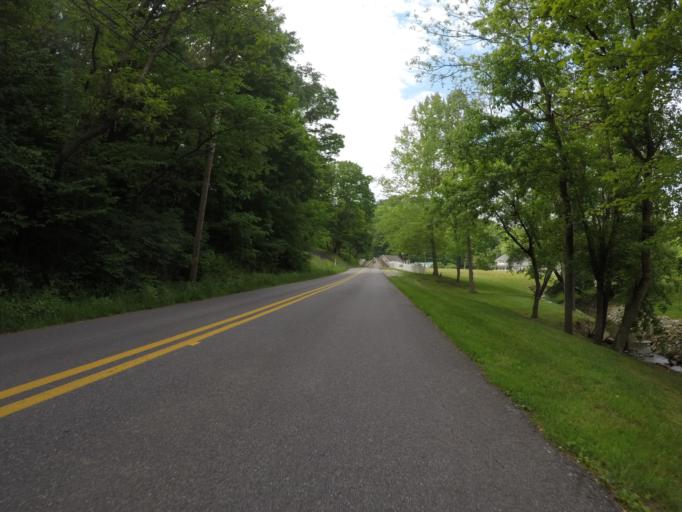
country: US
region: West Virginia
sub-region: Wayne County
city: Ceredo
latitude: 38.3503
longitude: -82.5628
